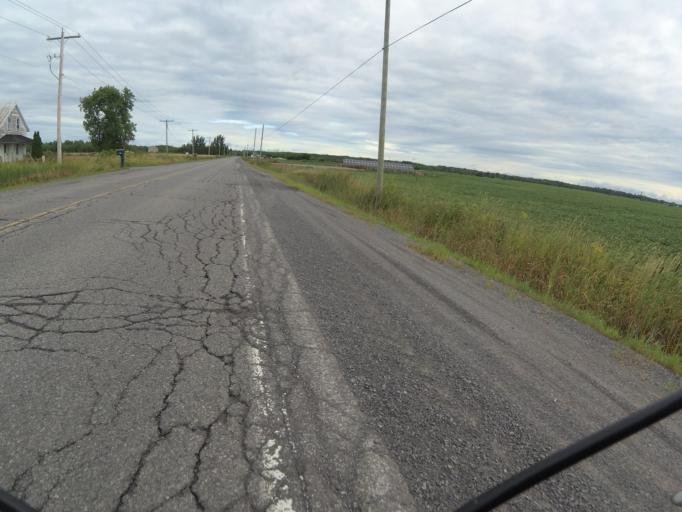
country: CA
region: Ontario
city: Bourget
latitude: 45.3791
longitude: -75.2722
